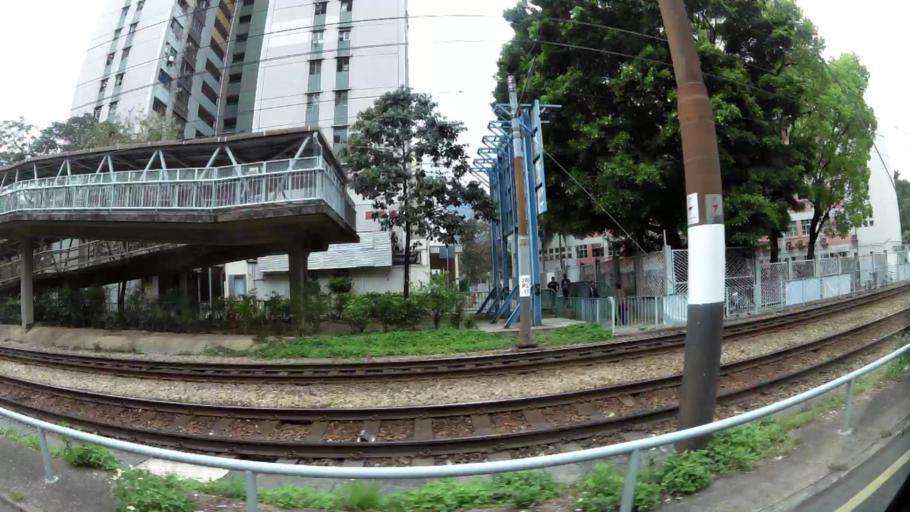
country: HK
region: Tuen Mun
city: Tuen Mun
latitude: 22.3892
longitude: 113.9751
